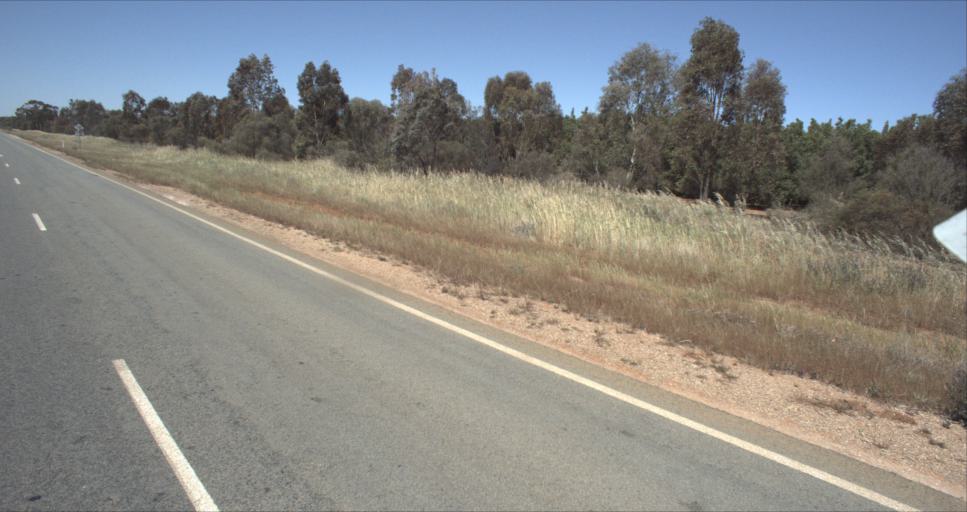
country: AU
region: New South Wales
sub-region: Leeton
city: Leeton
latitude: -34.5042
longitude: 146.4424
